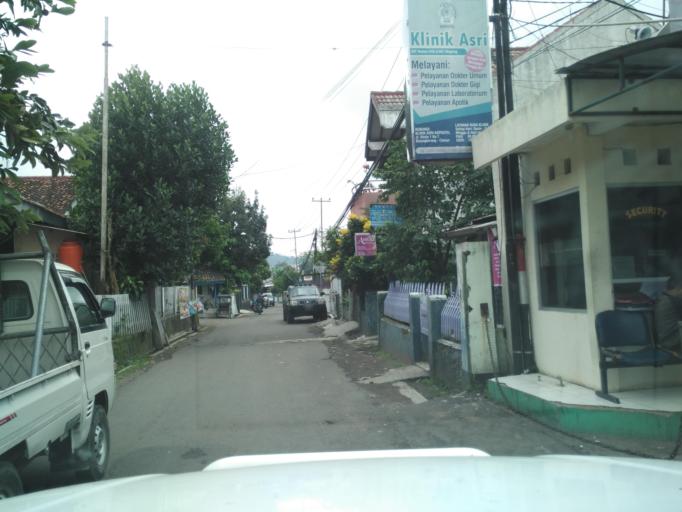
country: ID
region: West Java
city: Ciranjang-hilir
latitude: -6.8145
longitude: 107.1392
